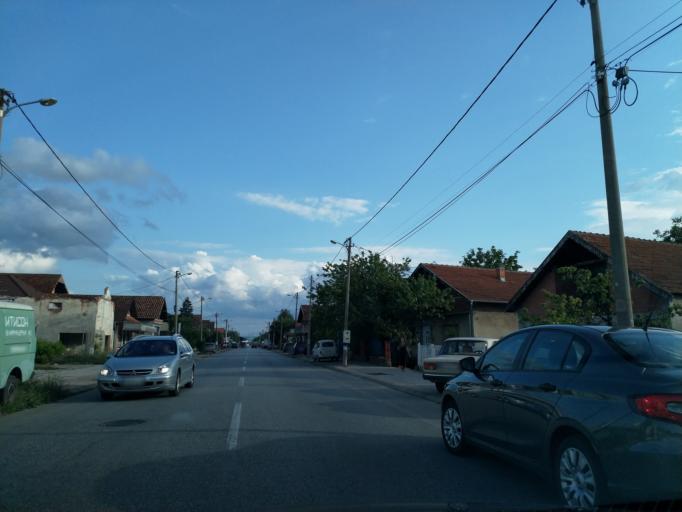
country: RS
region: Central Serbia
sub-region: Pomoravski Okrug
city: Paracin
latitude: 43.8499
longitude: 21.4135
